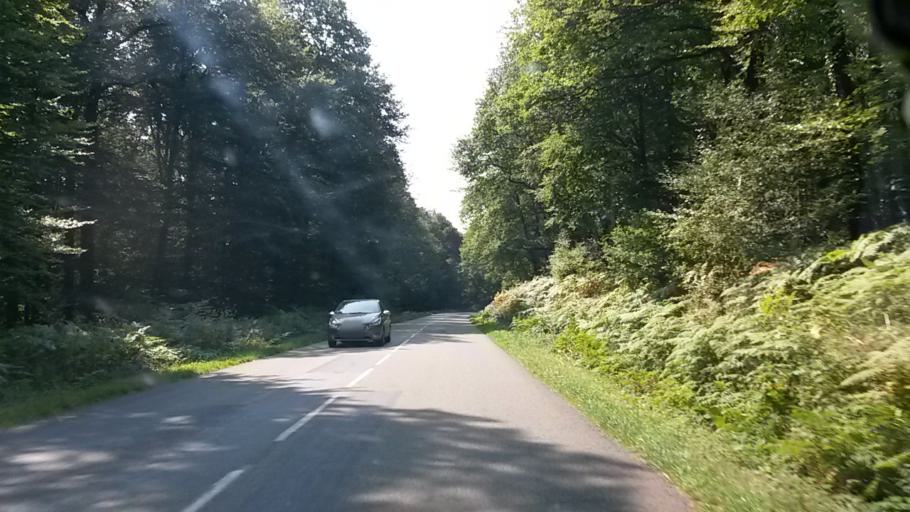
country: FR
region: Pays de la Loire
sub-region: Departement de la Mayenne
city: Courcite
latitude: 48.3706
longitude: -0.1885
